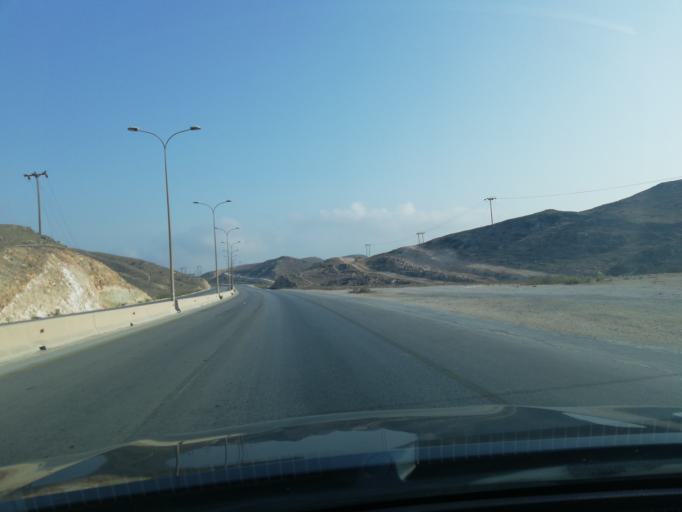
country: OM
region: Zufar
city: Salalah
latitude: 17.2729
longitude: 54.0827
